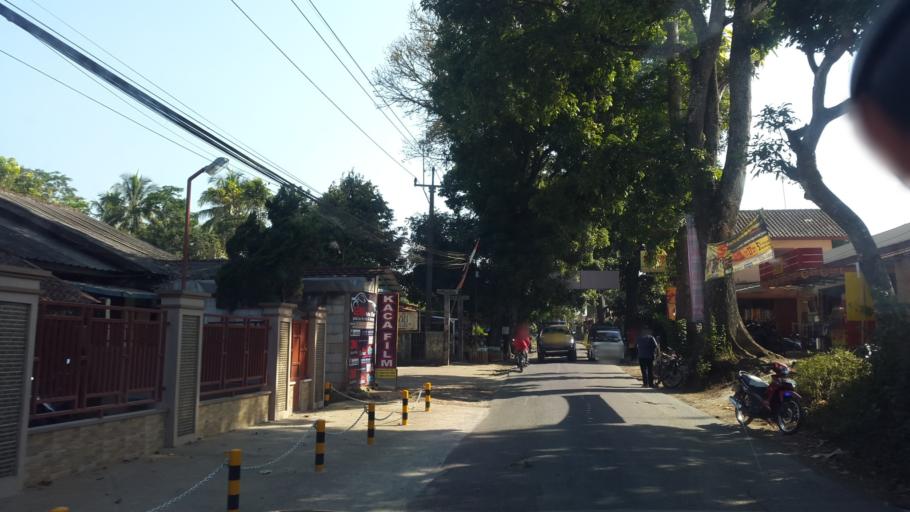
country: ID
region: West Java
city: Cicurug
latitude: -6.8672
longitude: 106.8045
